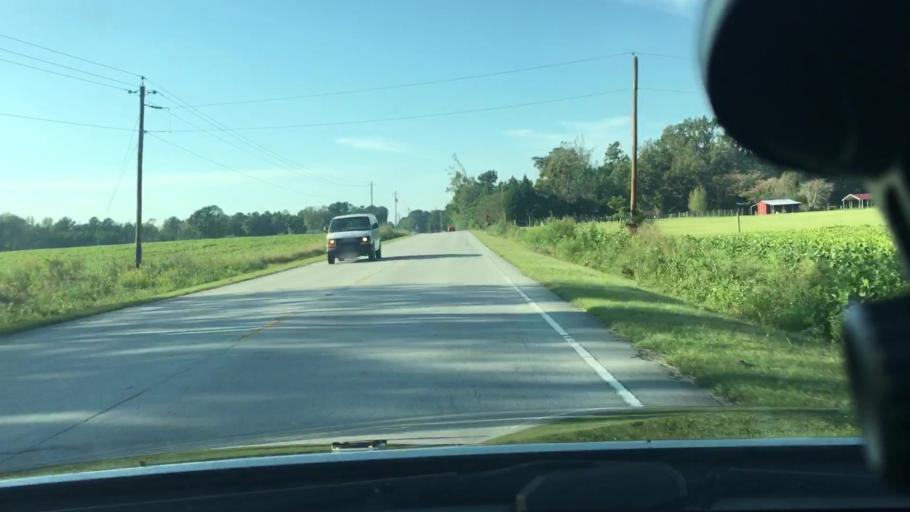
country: US
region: North Carolina
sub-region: Craven County
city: Vanceboro
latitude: 35.3382
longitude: -77.1753
